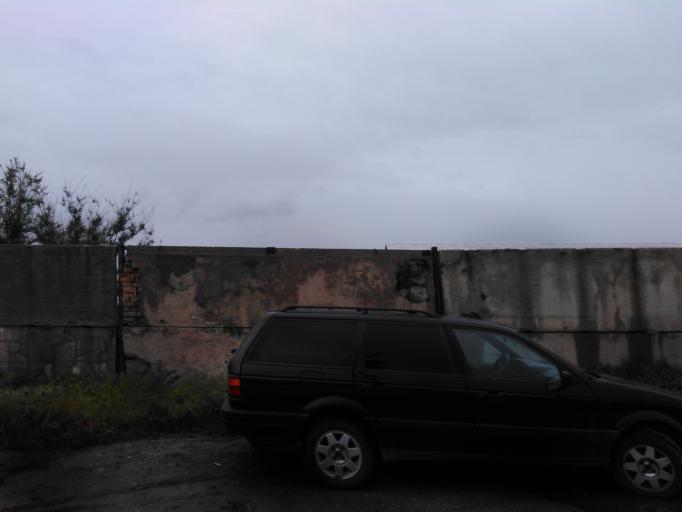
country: KG
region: Chuy
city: Tokmok
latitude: 42.8196
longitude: 75.3188
